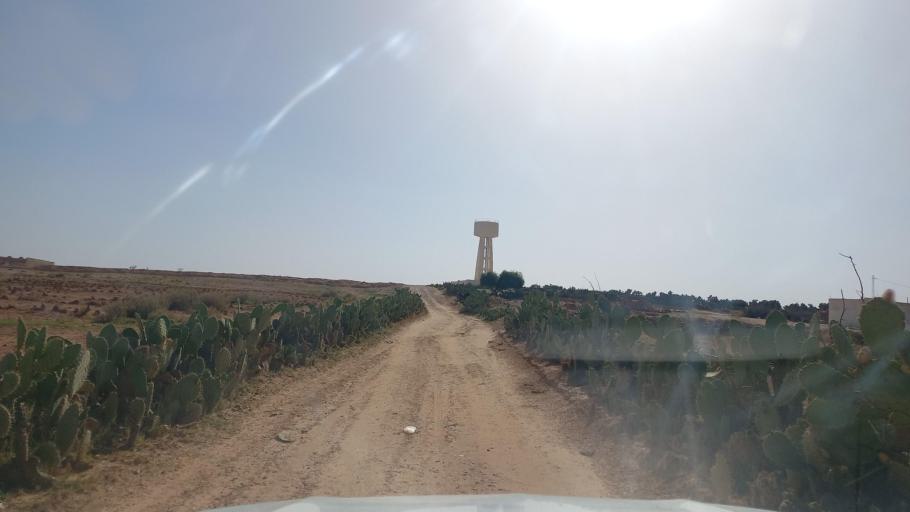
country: TN
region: Al Qasrayn
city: Sbiba
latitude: 35.3142
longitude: 9.0216
